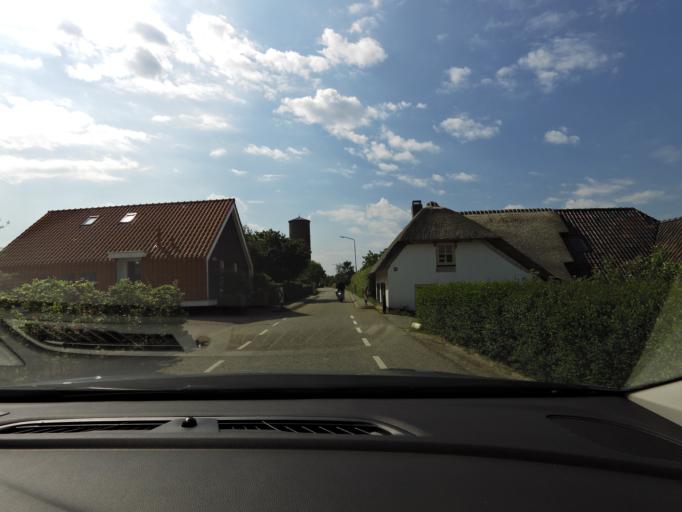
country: NL
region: North Brabant
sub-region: Gemeente Woudrichem
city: Almkerk
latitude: 51.7915
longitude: 4.9395
